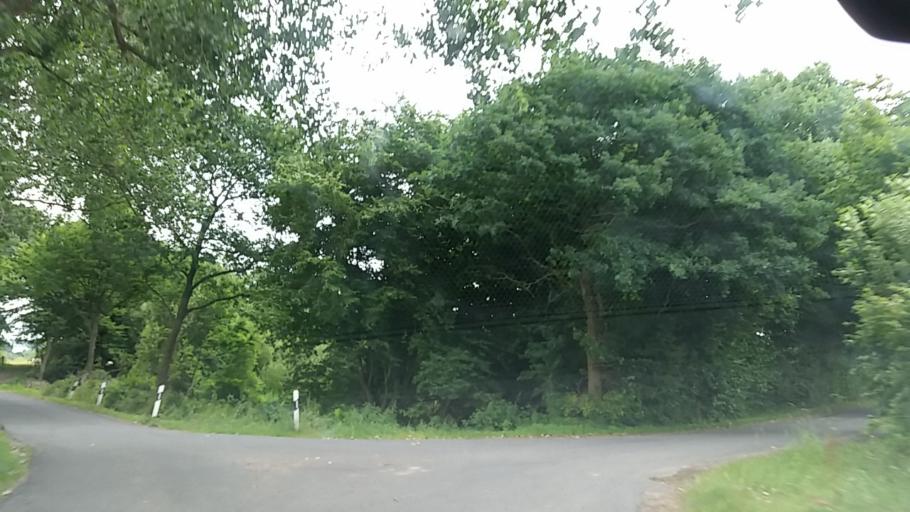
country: DE
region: Schleswig-Holstein
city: Dannewerk
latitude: 54.4996
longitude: 9.5198
